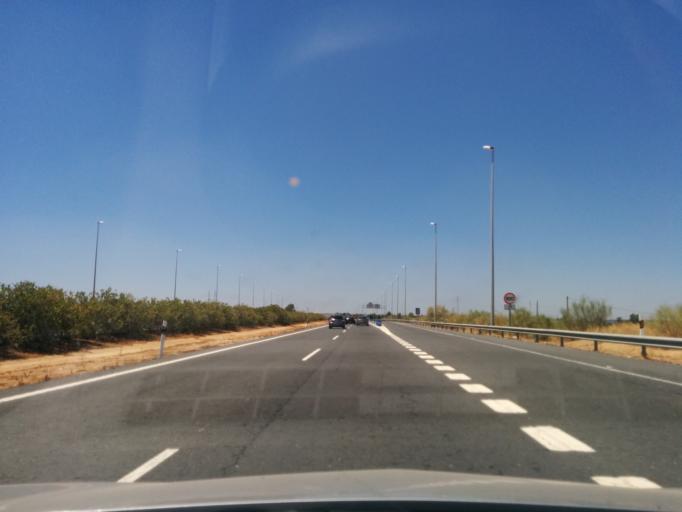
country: ES
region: Andalusia
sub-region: Provincia de Huelva
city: Gibraleon
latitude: 37.3568
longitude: -6.9506
